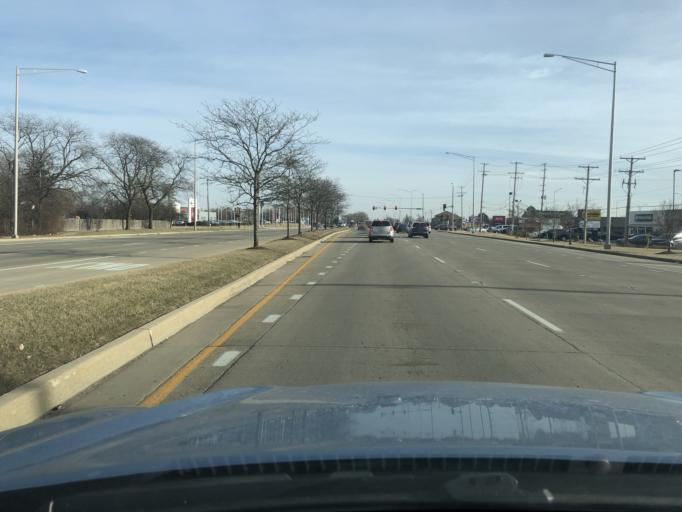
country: US
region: Illinois
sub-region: Cook County
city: Hoffman Estates
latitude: 42.0501
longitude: -88.1013
